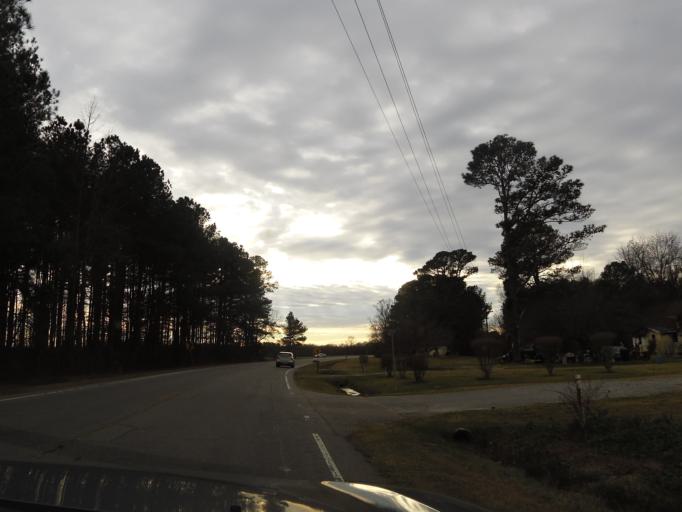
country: US
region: North Carolina
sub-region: Edgecombe County
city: Tarboro
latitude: 35.9659
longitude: -77.6285
